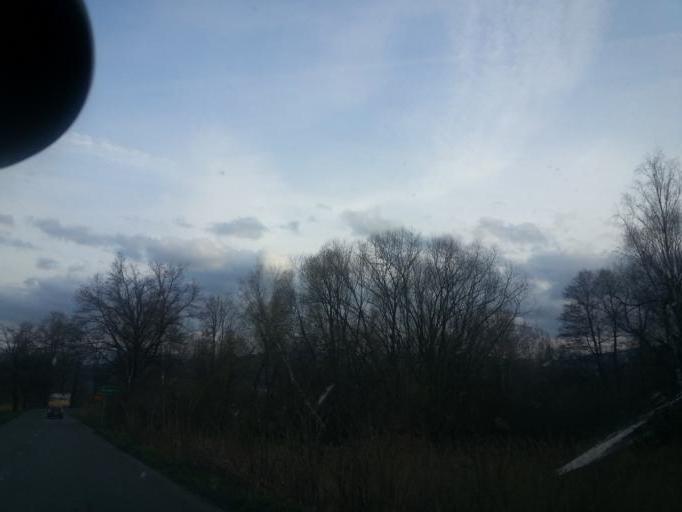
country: PL
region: Lower Silesian Voivodeship
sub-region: Jelenia Gora
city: Cieplice Slaskie Zdroj
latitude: 50.8503
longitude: 15.6860
